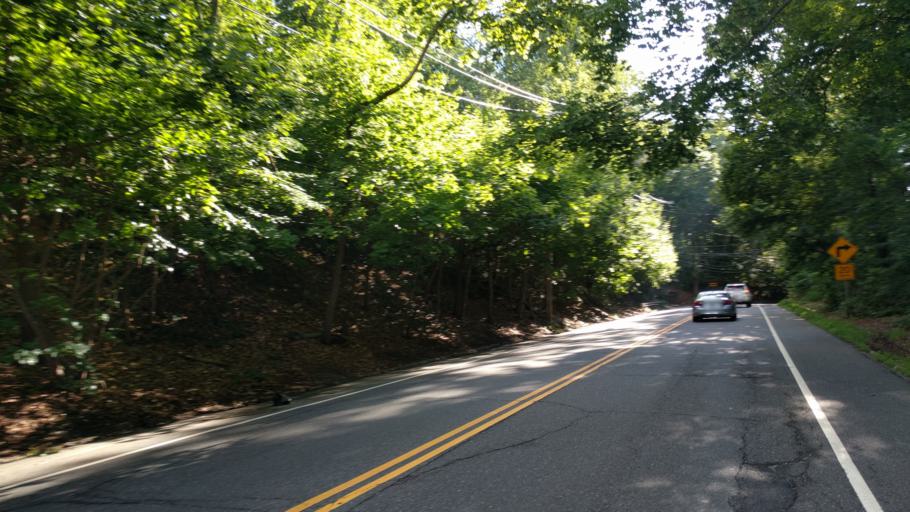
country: US
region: New York
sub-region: Nassau County
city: Oyster Bay Cove
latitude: 40.8709
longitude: -73.5100
